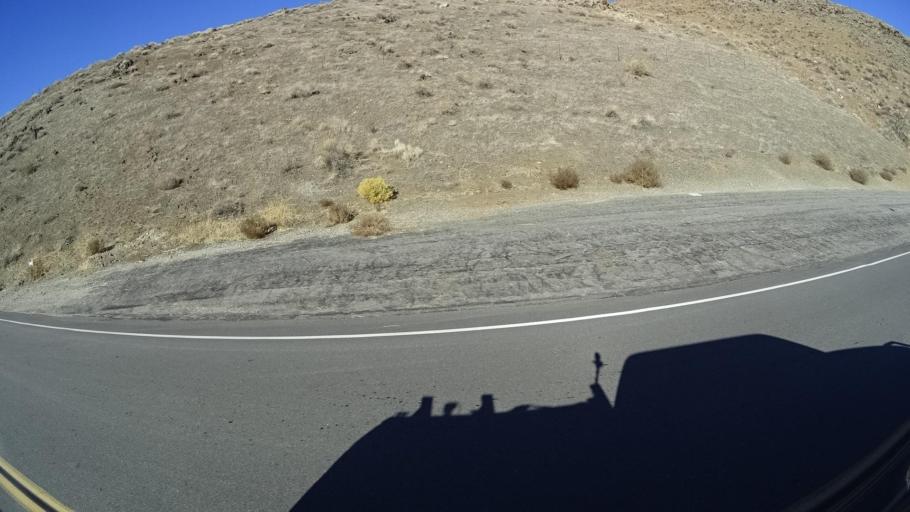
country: US
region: California
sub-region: Kern County
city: Wofford Heights
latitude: 35.6764
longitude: -118.4046
